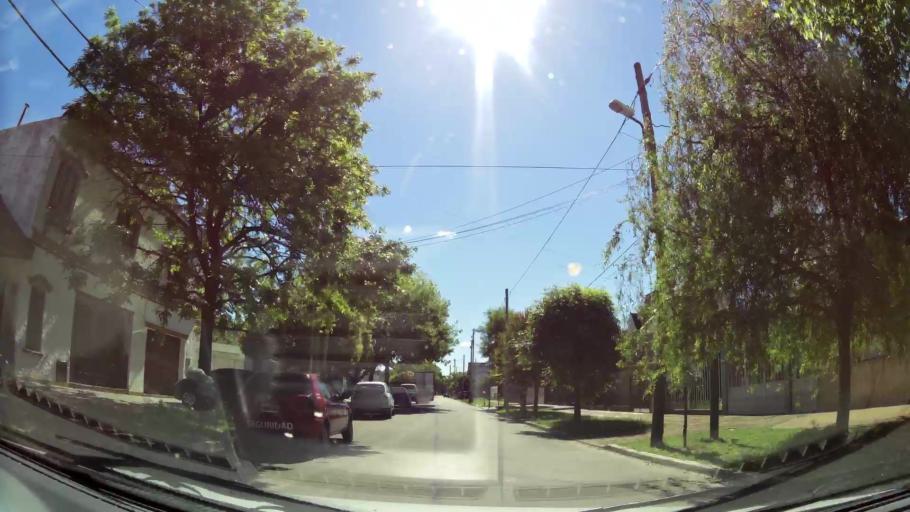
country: AR
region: Buenos Aires
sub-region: Partido de Lomas de Zamora
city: Lomas de Zamora
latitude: -34.7400
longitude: -58.4148
